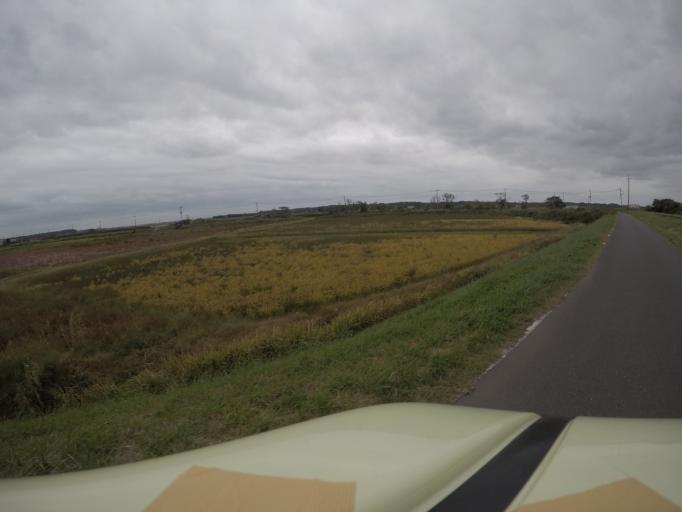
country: JP
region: Ibaraki
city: Inashiki
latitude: 35.9902
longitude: 140.4019
